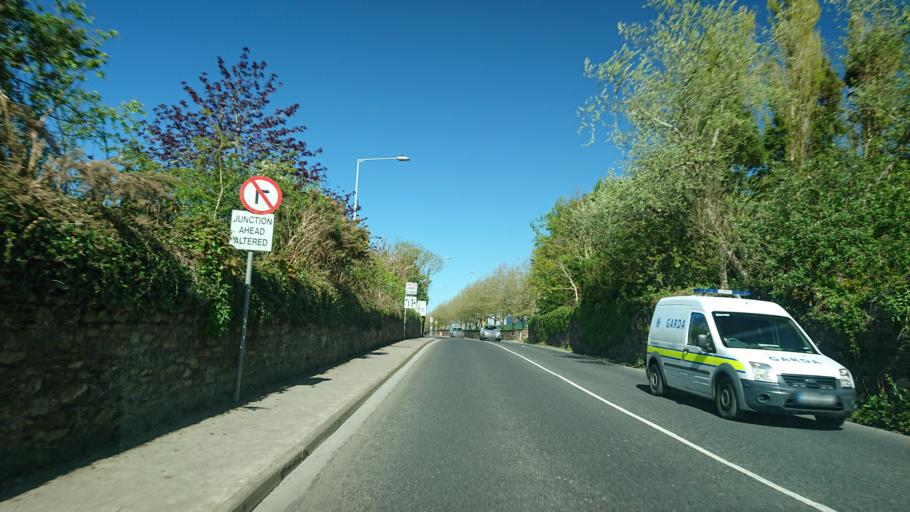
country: IE
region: Munster
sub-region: Waterford
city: Waterford
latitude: 52.2465
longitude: -7.0758
